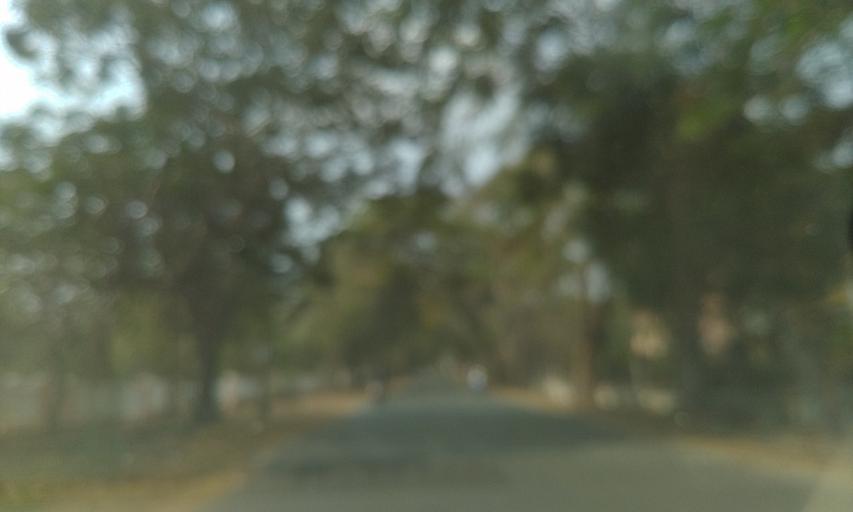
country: IN
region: Goa
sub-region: North Goa
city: Panaji
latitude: 15.4867
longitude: 73.8259
